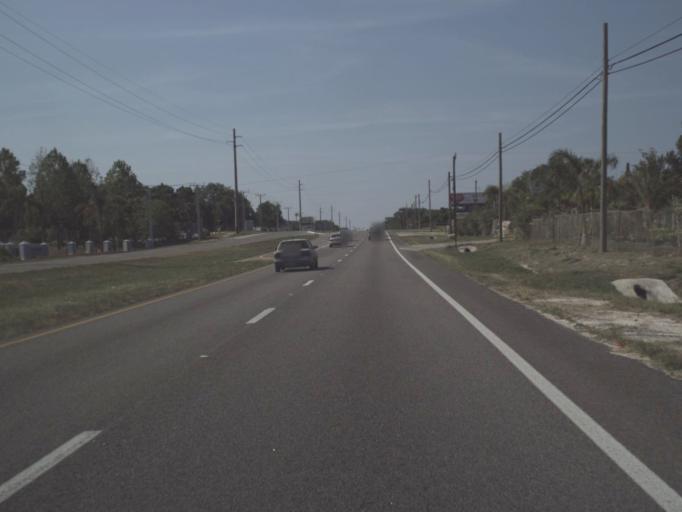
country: US
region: Florida
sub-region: Brevard County
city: Sharpes
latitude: 28.4182
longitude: -80.7557
